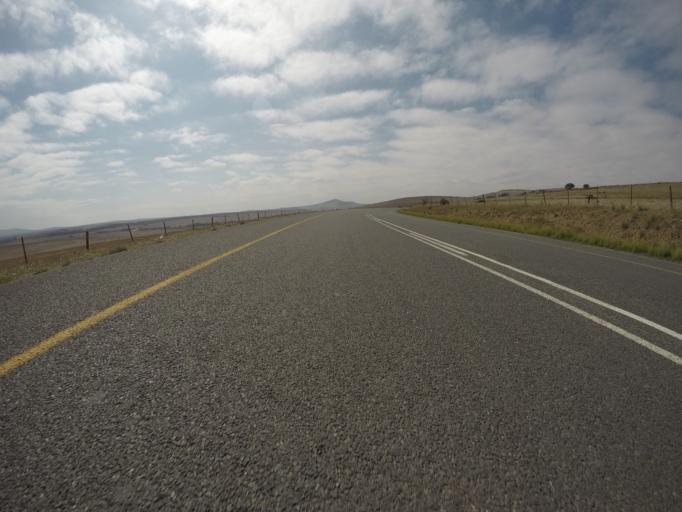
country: ZA
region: Western Cape
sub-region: City of Cape Town
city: Sunset Beach
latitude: -33.7925
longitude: 18.5712
